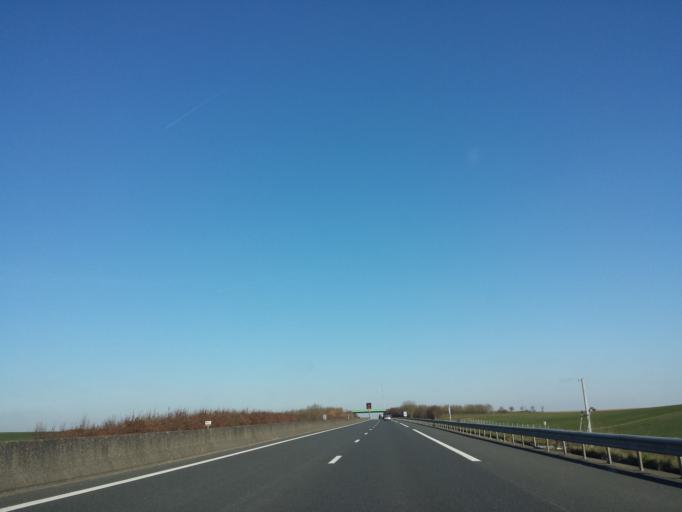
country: FR
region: Picardie
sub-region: Departement de l'Oise
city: Tille
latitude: 49.5506
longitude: 2.1902
